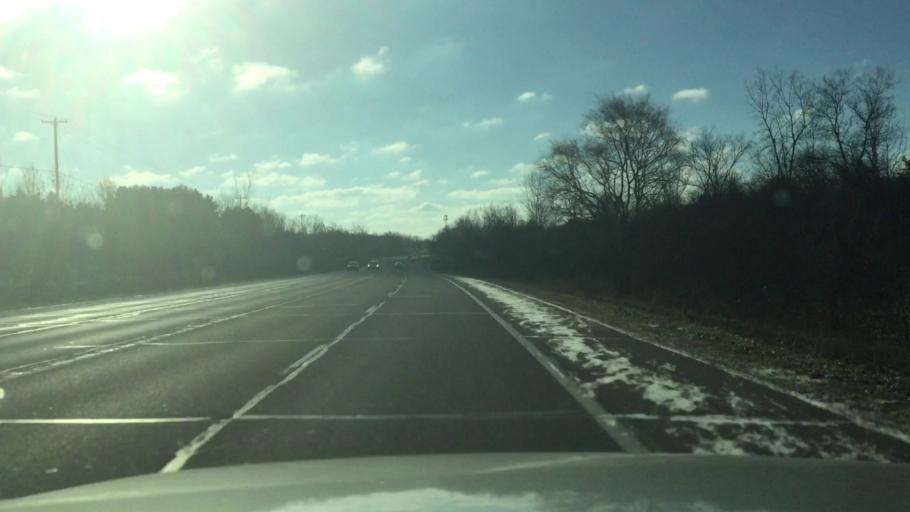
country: US
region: Michigan
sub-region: Genesee County
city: Grand Blanc
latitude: 42.9198
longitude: -83.6502
